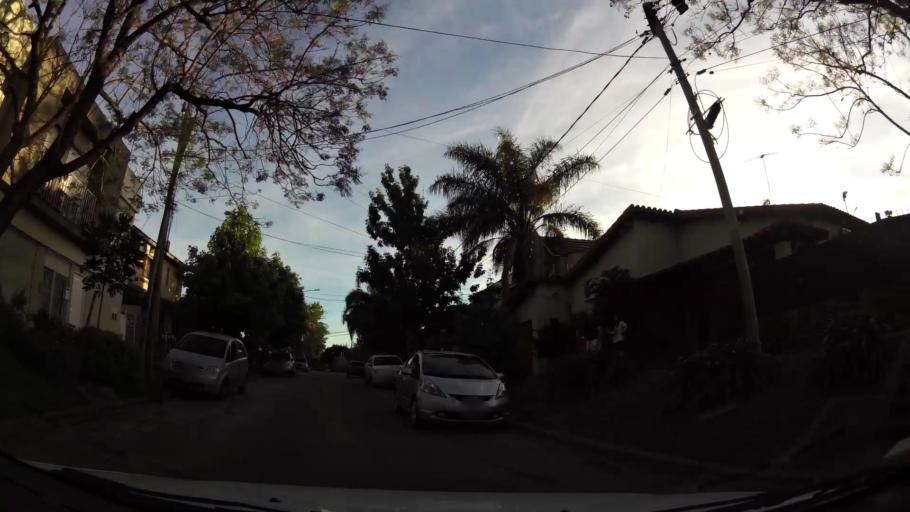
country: AR
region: Buenos Aires
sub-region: Partido de Moron
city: Moron
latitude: -34.6409
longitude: -58.6377
